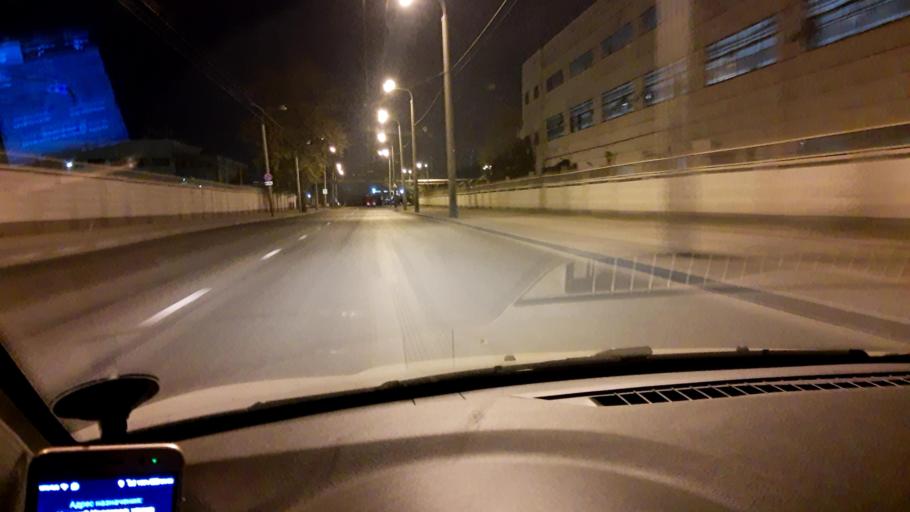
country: RU
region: Nizjnij Novgorod
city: Nizhniy Novgorod
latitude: 56.2474
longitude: 43.9132
